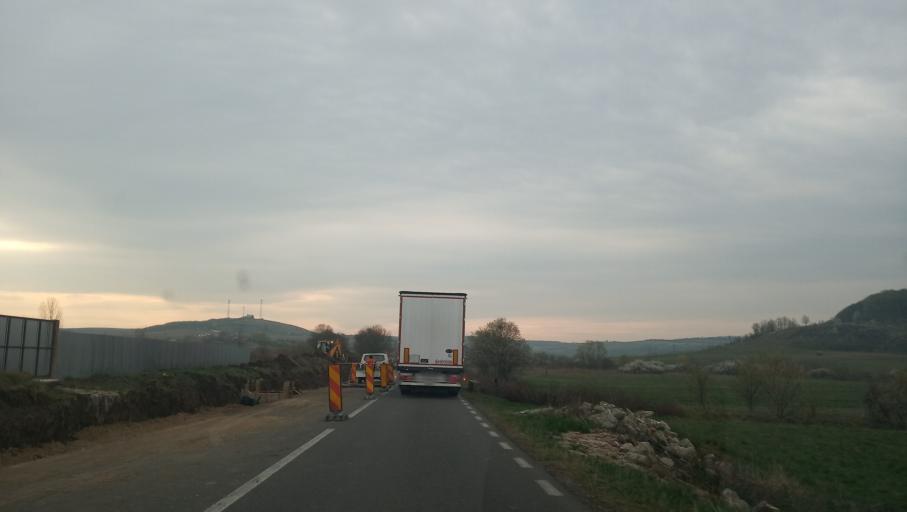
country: RO
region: Bihor
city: Hidiselu de Sus
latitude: 46.9430
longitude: 22.0309
